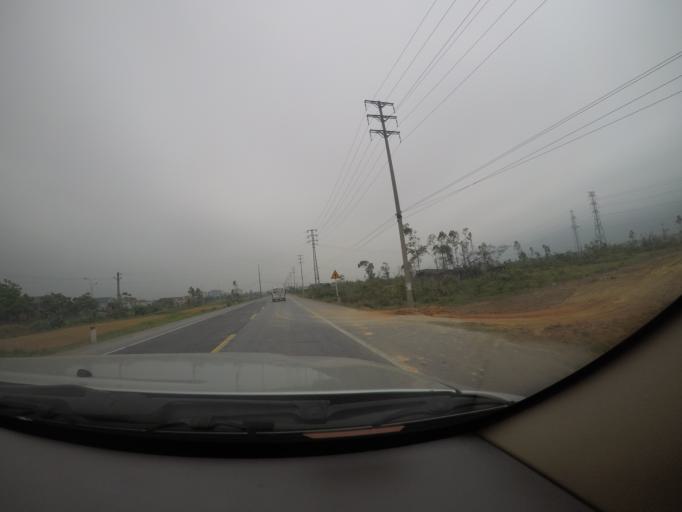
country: VN
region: Ha Tinh
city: Ky Anh
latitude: 18.0219
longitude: 106.3709
